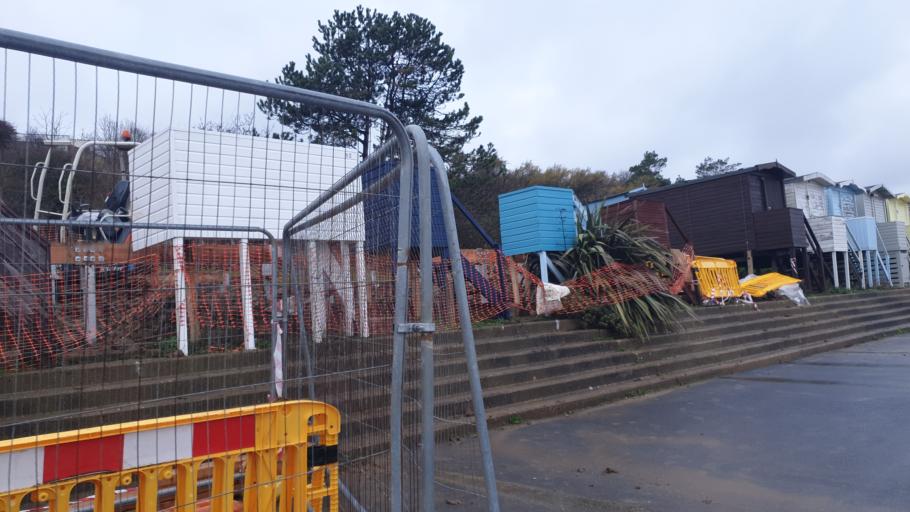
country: GB
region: England
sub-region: Essex
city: Walton-on-the-Naze
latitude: 51.8400
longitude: 1.2618
